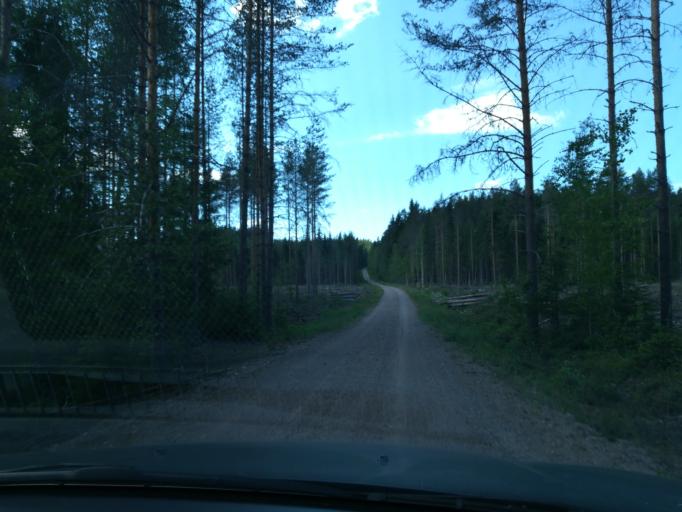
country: FI
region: South Karelia
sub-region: Imatra
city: Ruokolahti
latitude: 61.5392
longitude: 28.8177
